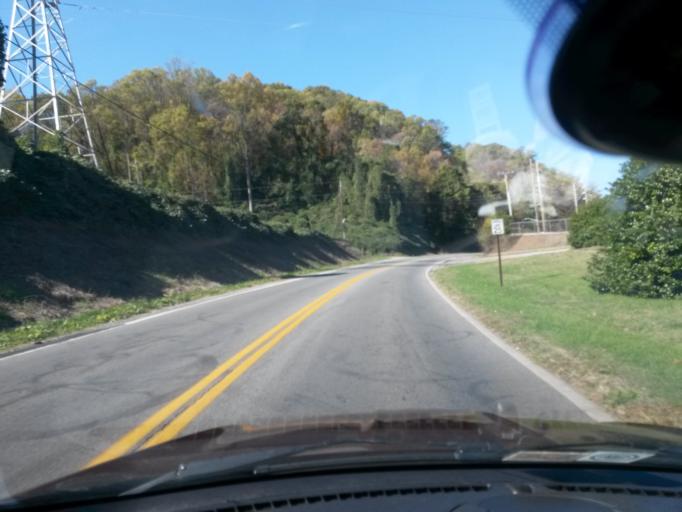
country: US
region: Virginia
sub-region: City of Roanoke
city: Cedar Bluff
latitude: 37.2495
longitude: -79.9208
